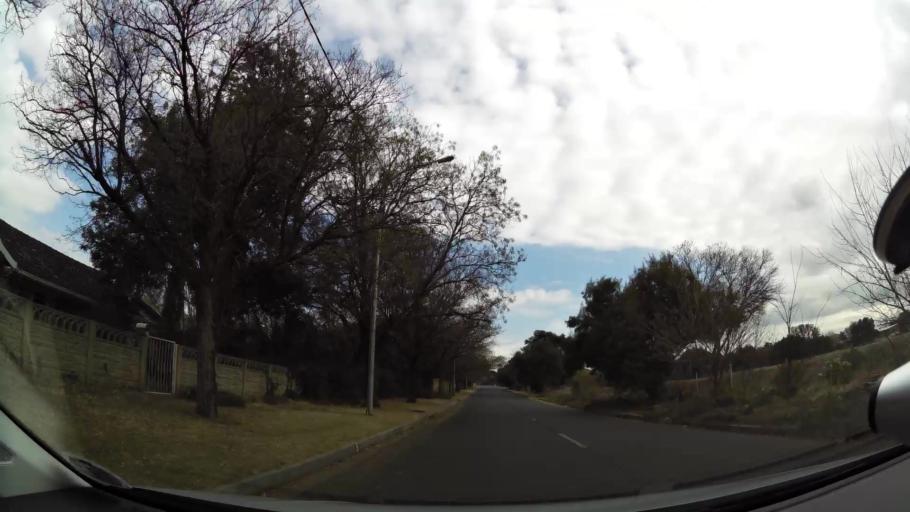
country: ZA
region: Orange Free State
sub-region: Fezile Dabi District Municipality
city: Kroonstad
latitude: -27.6366
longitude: 27.2375
